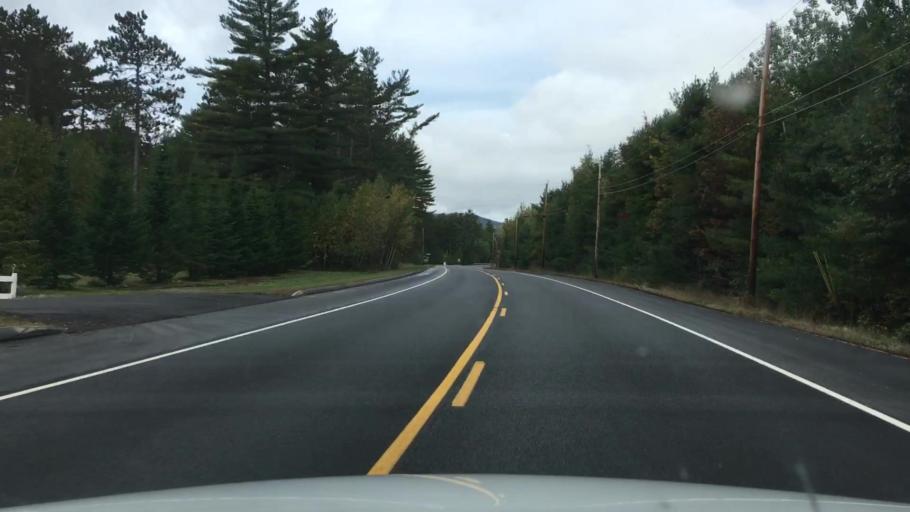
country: US
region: Maine
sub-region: Oxford County
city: Bethel
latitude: 44.4012
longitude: -70.8650
